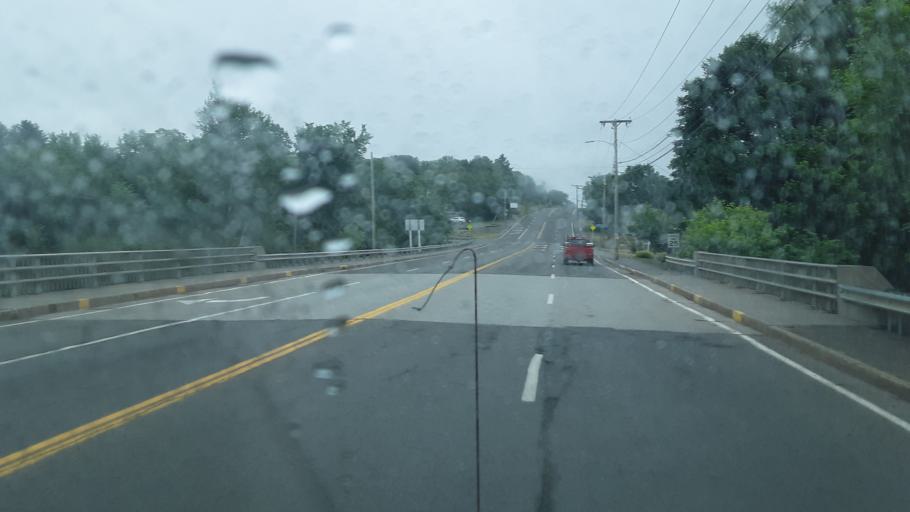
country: US
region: Maine
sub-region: Penobscot County
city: Millinocket
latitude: 45.6574
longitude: -68.7049
